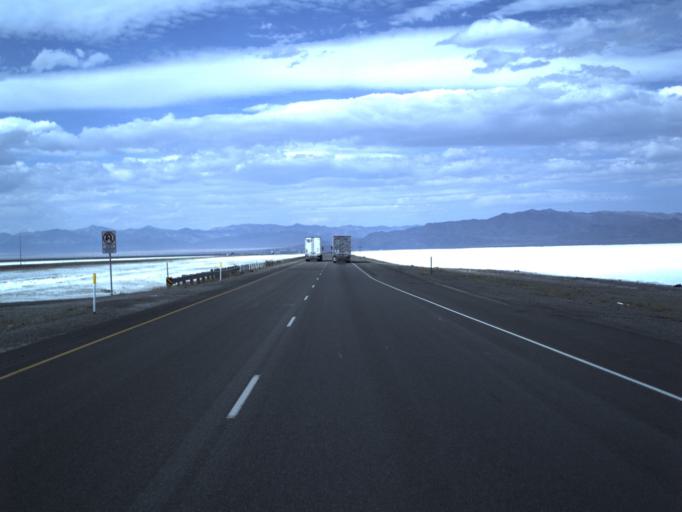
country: US
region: Utah
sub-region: Tooele County
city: Wendover
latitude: 40.7395
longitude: -113.8584
